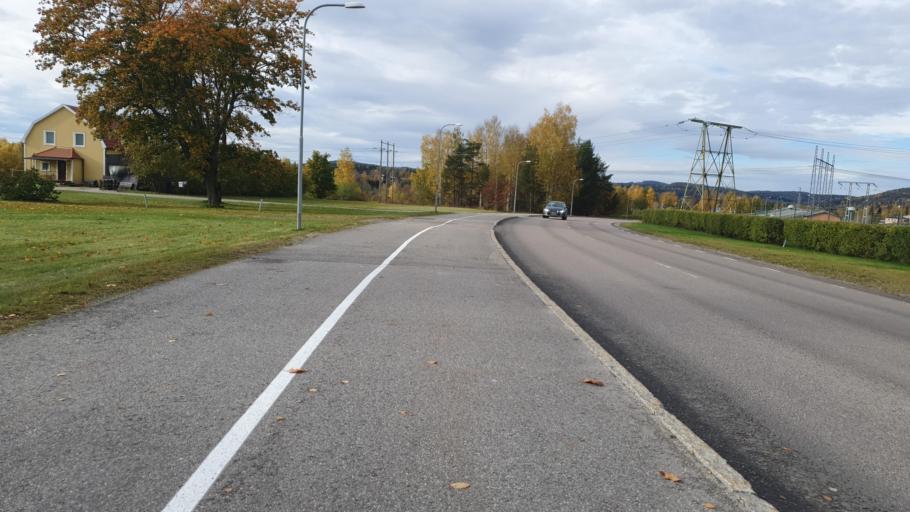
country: SE
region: Vaesternorrland
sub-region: Sundsvalls Kommun
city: Sundsvall
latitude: 62.4053
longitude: 17.2399
